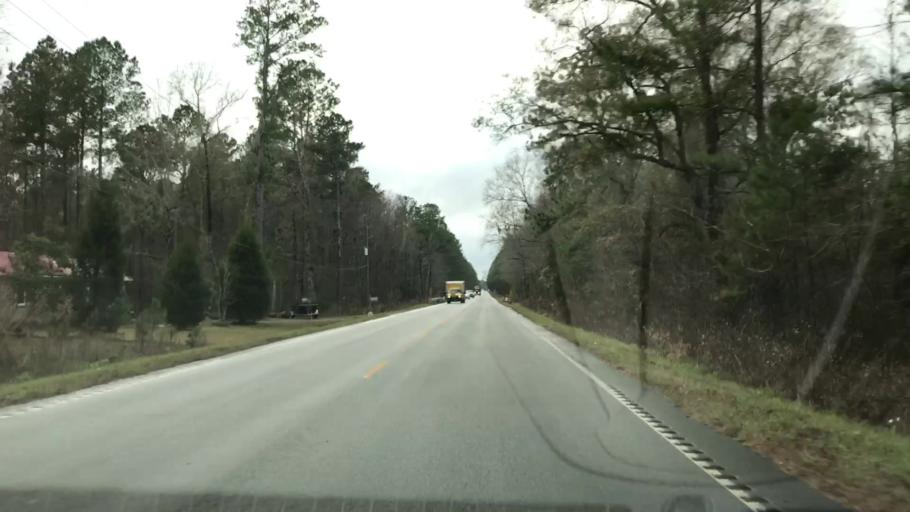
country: US
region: South Carolina
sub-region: Williamsburg County
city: Andrews
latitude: 33.2845
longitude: -79.7127
